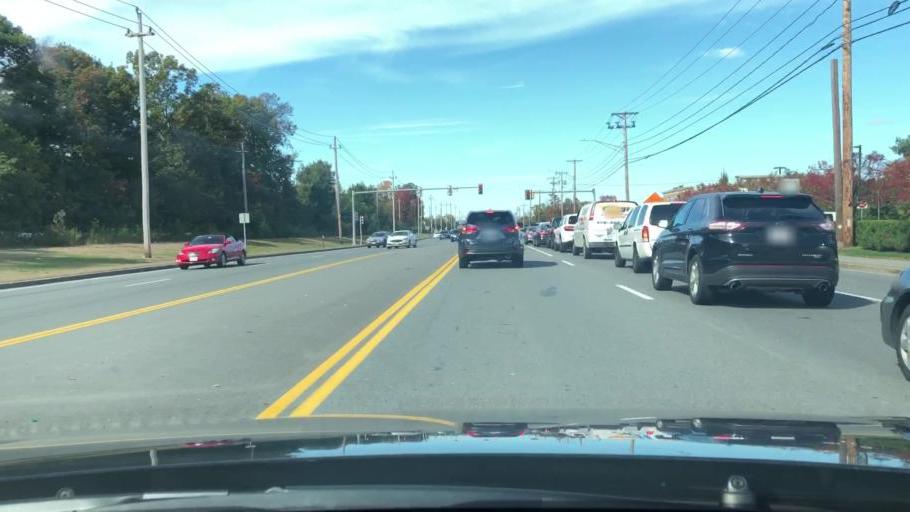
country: US
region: New Hampshire
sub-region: Rockingham County
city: Salem
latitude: 42.7621
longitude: -71.2150
